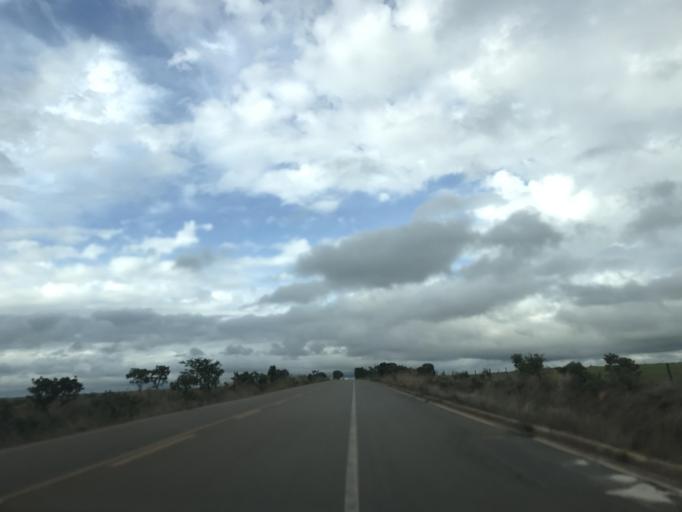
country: BR
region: Goias
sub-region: Vianopolis
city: Vianopolis
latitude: -16.5741
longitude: -48.2944
